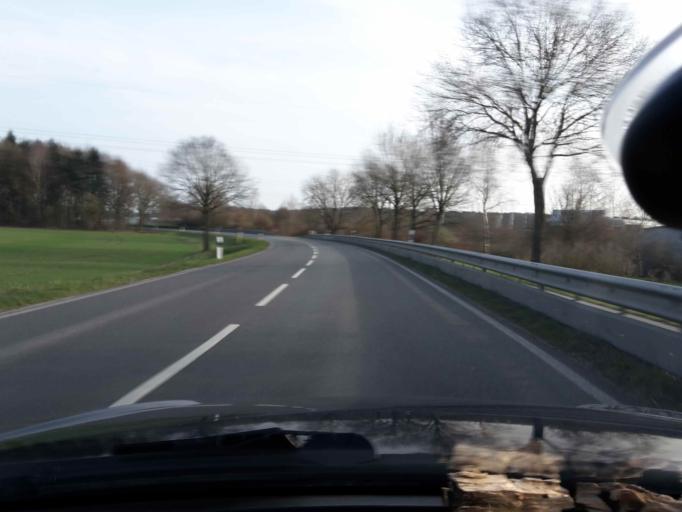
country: DE
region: Lower Saxony
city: Buchholz in der Nordheide
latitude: 53.3555
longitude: 9.8753
